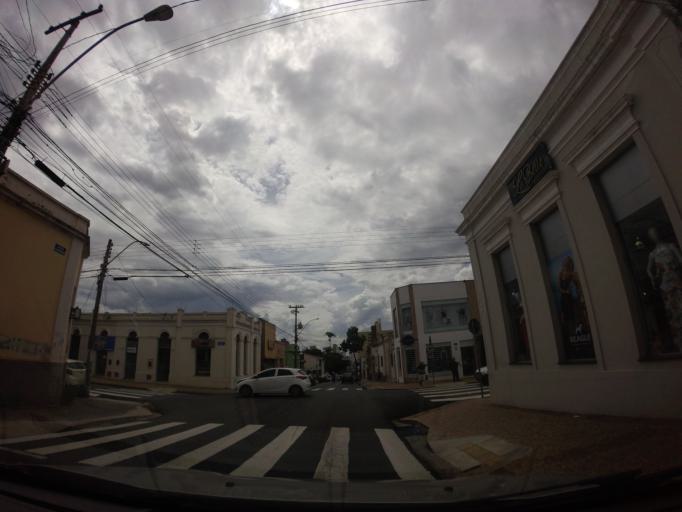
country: BR
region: Sao Paulo
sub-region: Piracicaba
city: Piracicaba
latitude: -22.7296
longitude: -47.6424
